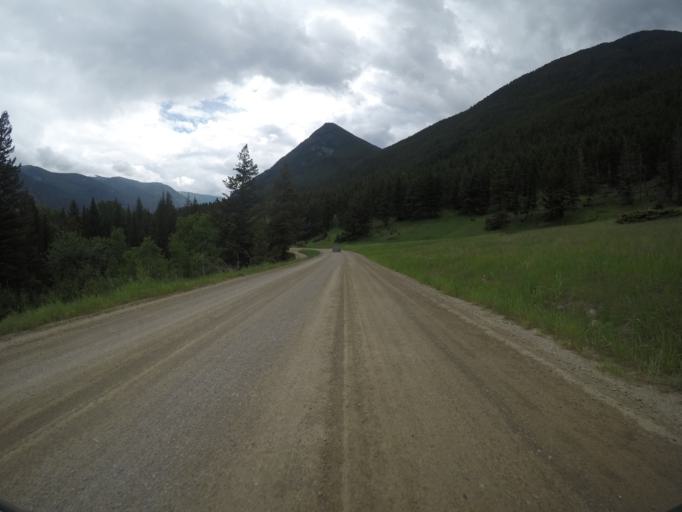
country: US
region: Montana
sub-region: Park County
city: Livingston
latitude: 45.4935
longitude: -110.2258
